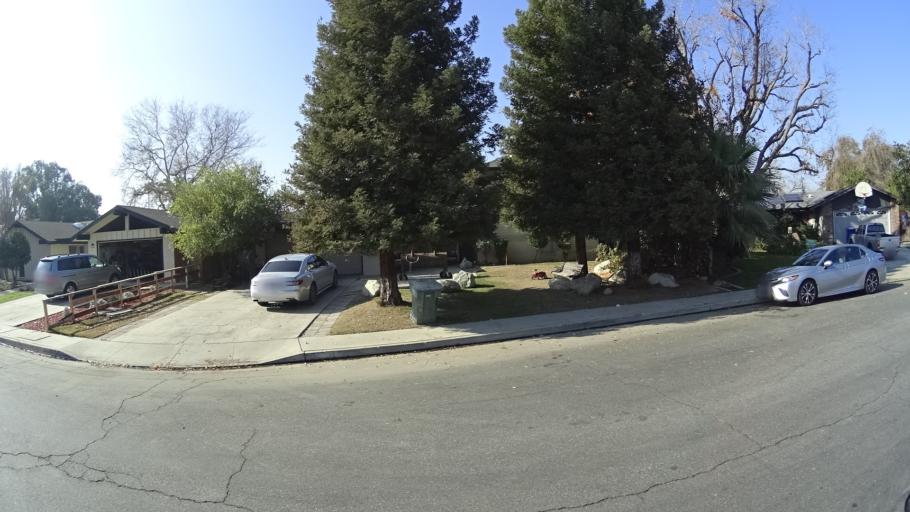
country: US
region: California
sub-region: Kern County
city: Greenacres
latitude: 35.3596
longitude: -119.0740
